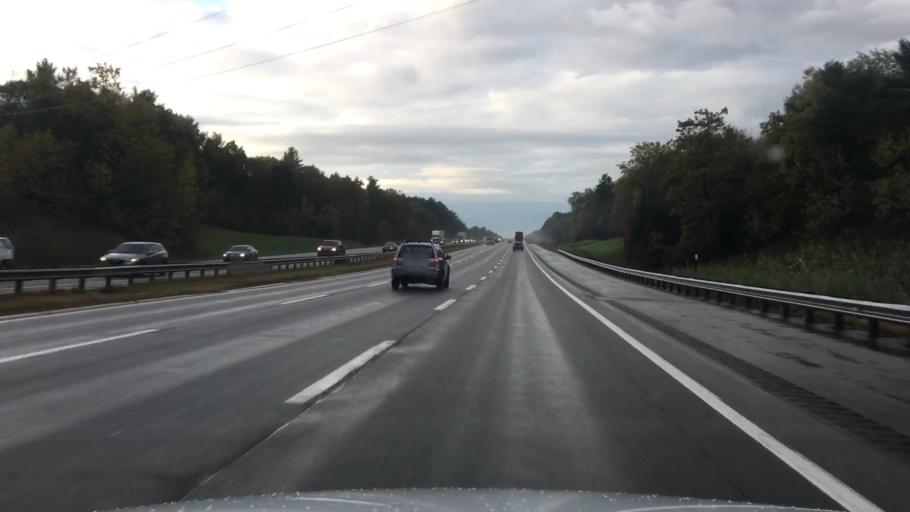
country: US
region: Maine
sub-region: Cumberland County
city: West Scarborough
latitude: 43.5843
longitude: -70.3930
